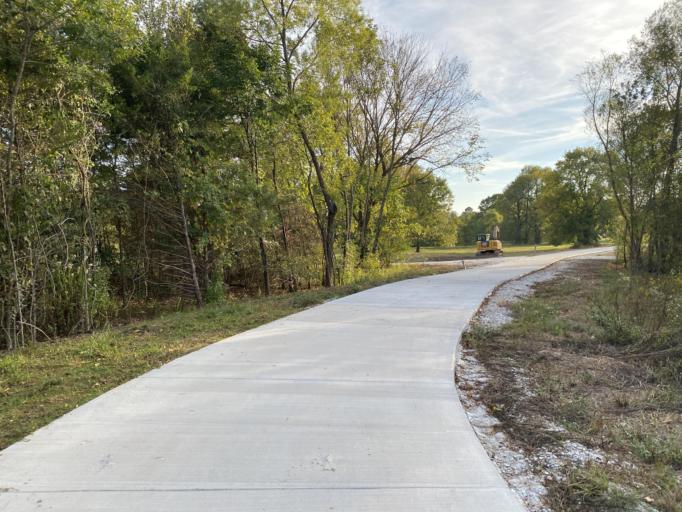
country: US
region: Arkansas
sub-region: Washington County
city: Johnson
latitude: 36.1058
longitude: -94.1943
